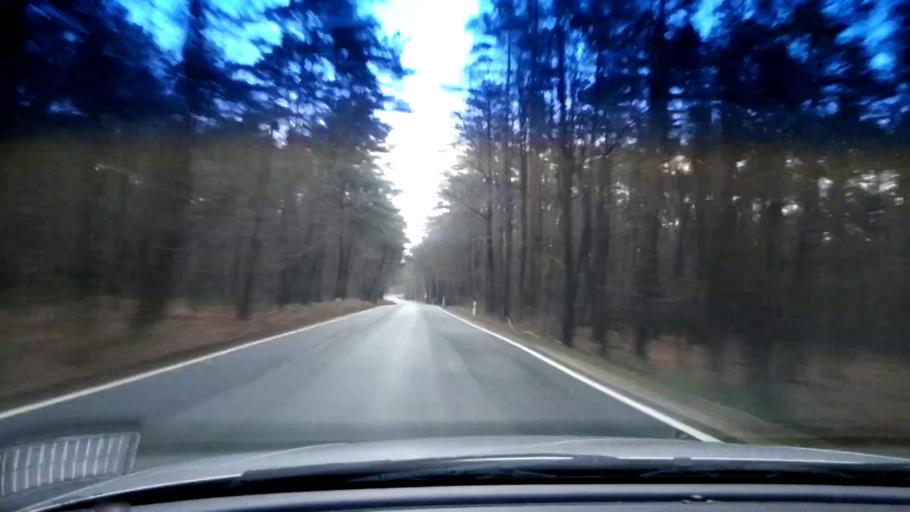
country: DE
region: Bavaria
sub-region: Upper Franconia
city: Burgebrach
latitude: 49.8657
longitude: 10.7396
